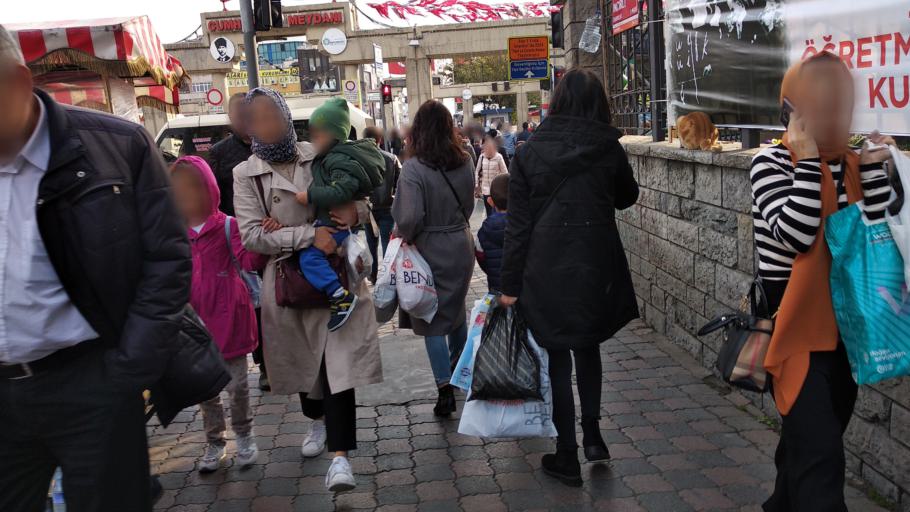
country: TR
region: Istanbul
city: Bahcelievler
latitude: 40.9814
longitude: 28.8736
